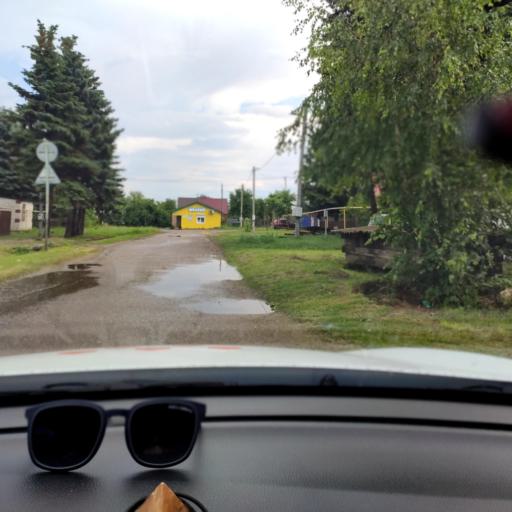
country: RU
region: Tatarstan
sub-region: Zelenodol'skiy Rayon
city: Vasil'yevo
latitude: 55.8265
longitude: 48.7187
